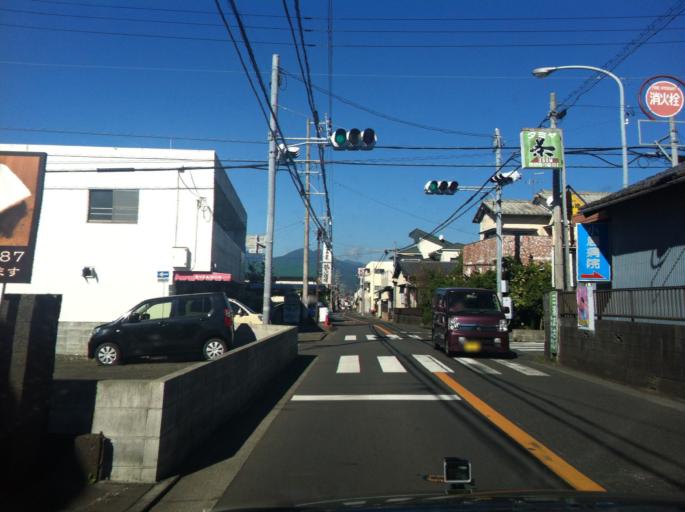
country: JP
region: Shizuoka
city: Shizuoka-shi
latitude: 34.9759
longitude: 138.4263
